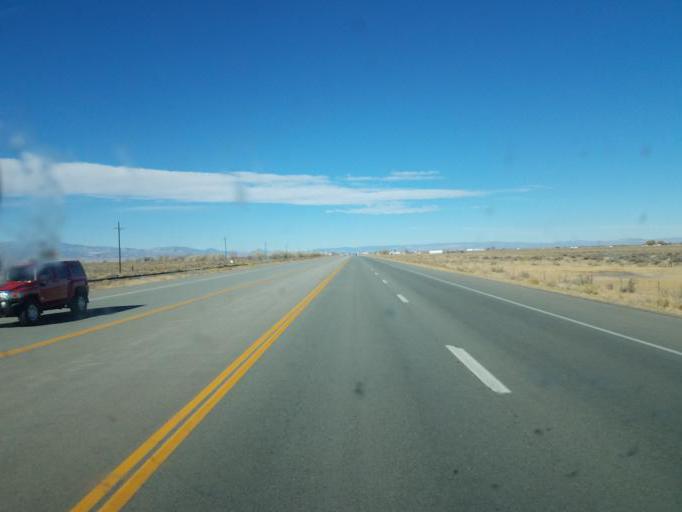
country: US
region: Colorado
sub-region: Alamosa County
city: Alamosa
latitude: 37.5158
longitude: -105.9901
